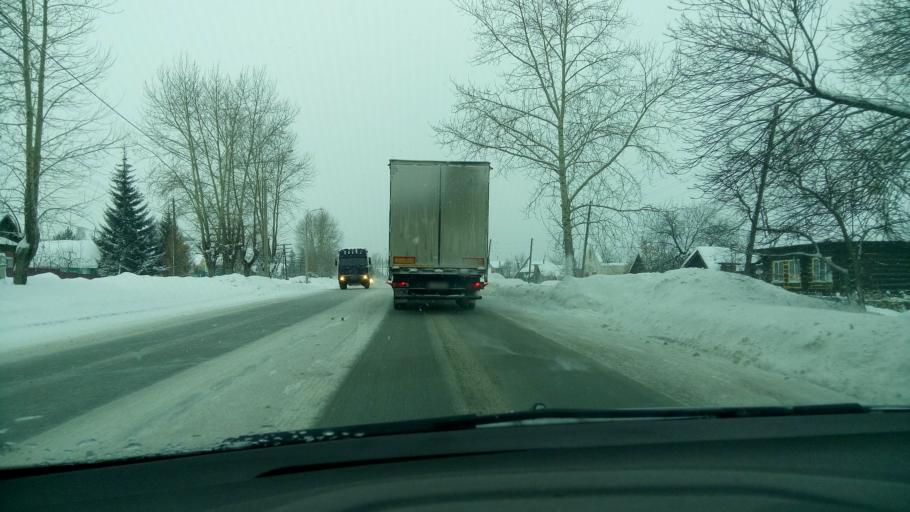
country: RU
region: Sverdlovsk
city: Beloyarskiy
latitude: 56.7572
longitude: 61.3673
